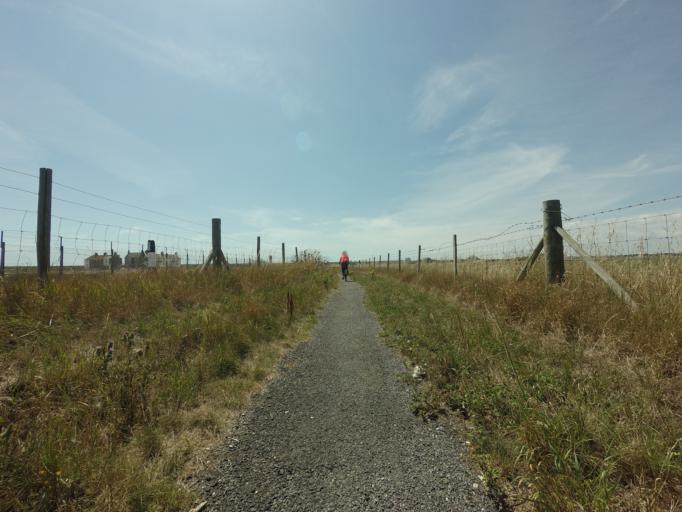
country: GB
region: England
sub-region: Kent
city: Lydd
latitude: 50.9296
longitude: 0.8344
